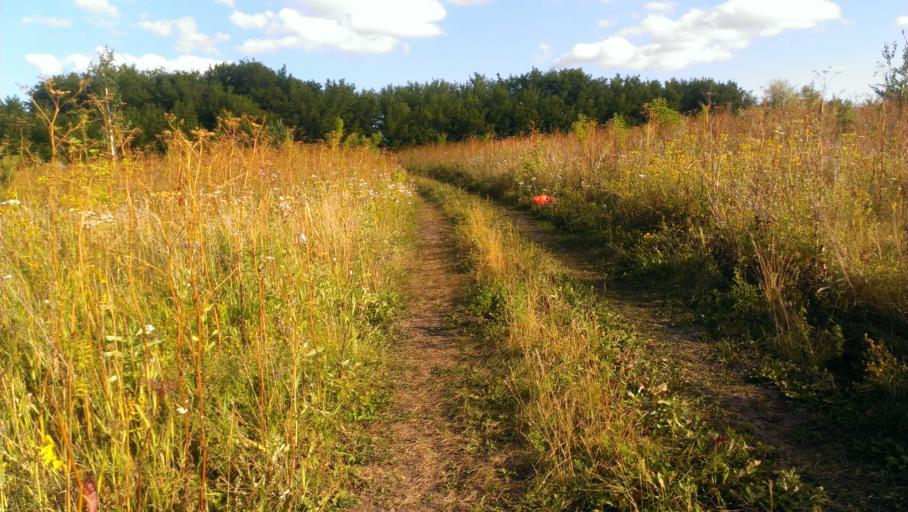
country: RU
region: Altai Krai
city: Gon'ba
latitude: 53.3880
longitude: 83.5992
